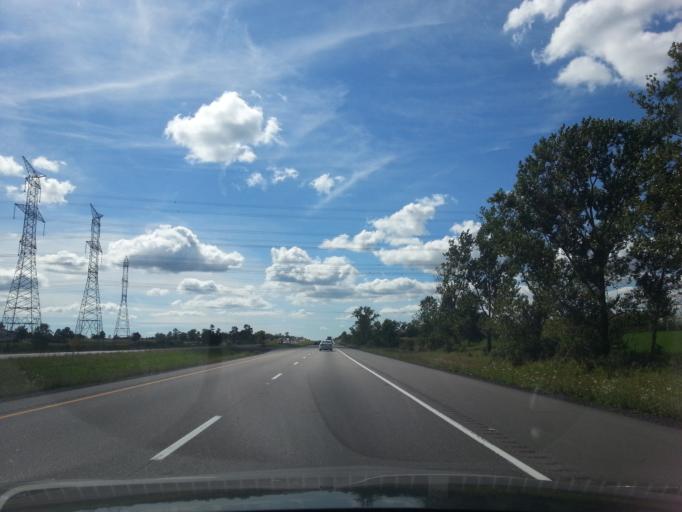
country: CA
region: Ontario
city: Napanee Downtown
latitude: 44.2520
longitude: -77.0095
